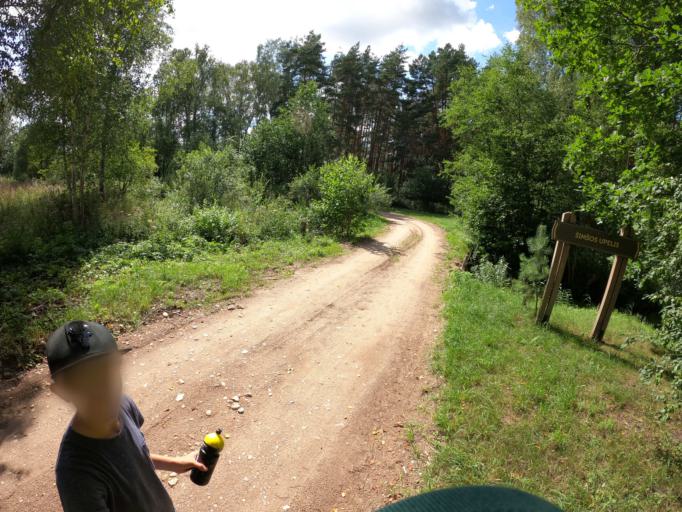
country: LT
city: Tytuveneliai
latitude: 55.6632
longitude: 23.2049
